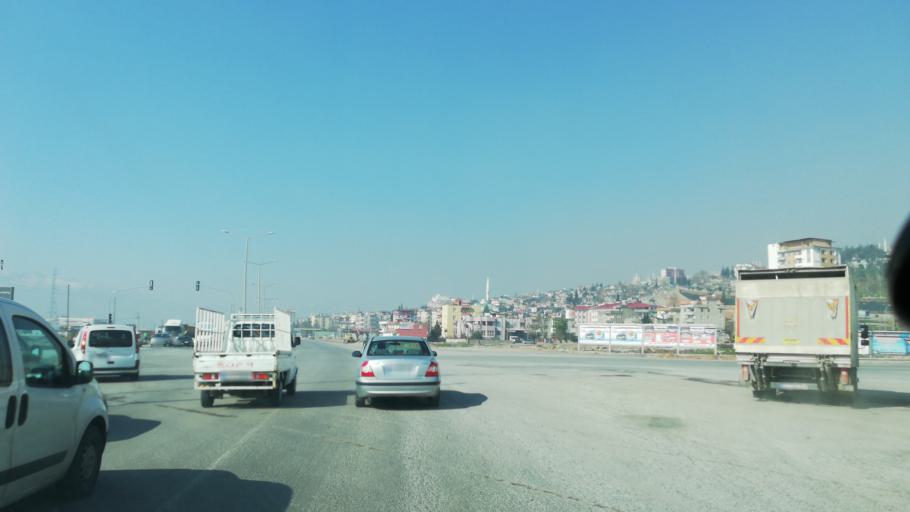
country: TR
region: Kahramanmaras
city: Kahramanmaras
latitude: 37.5695
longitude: 36.9178
